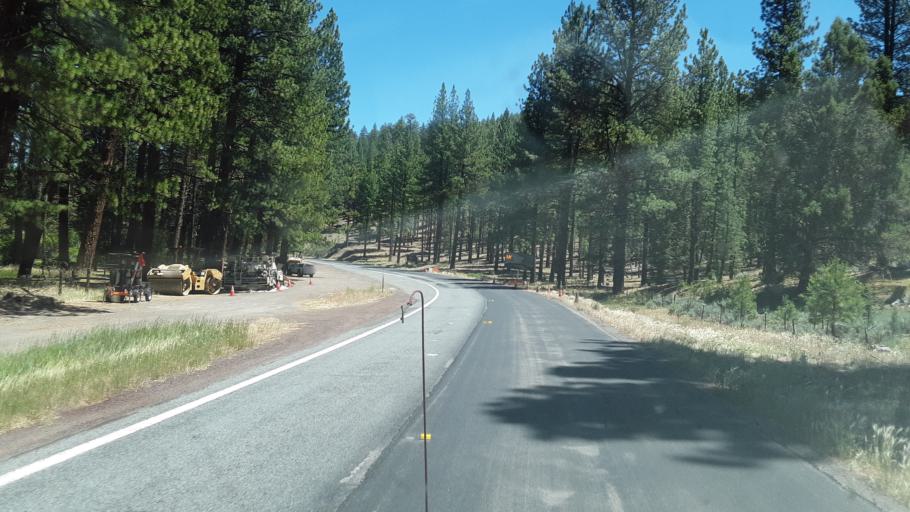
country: US
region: California
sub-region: Modoc County
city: Alturas
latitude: 41.0131
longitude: -120.8319
